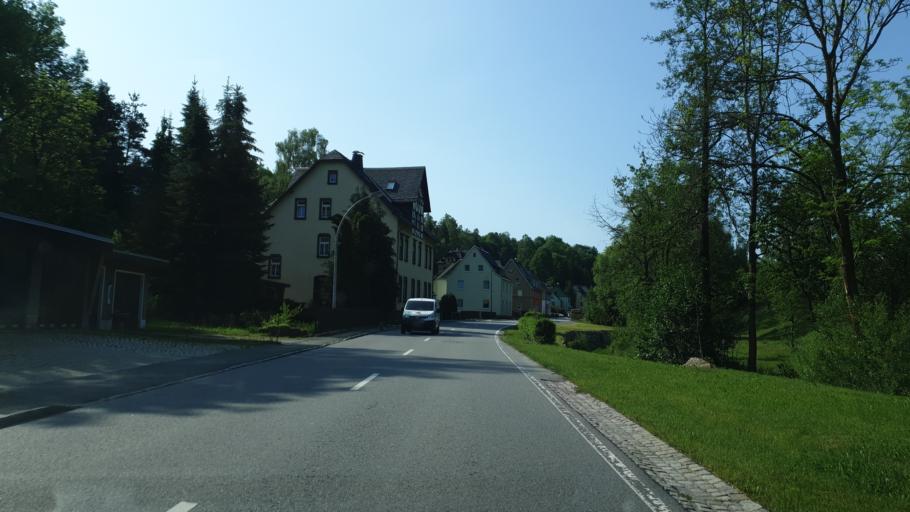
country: DE
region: Saxony
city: Zschorlau
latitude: 50.5776
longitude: 12.6577
